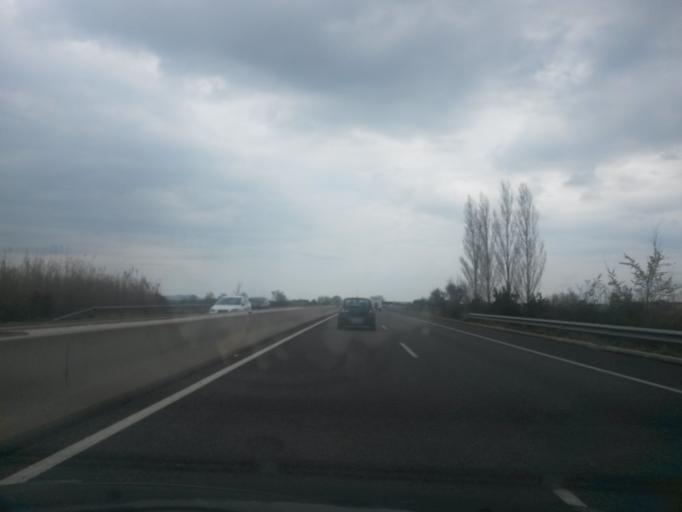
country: ES
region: Catalonia
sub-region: Provincia de Girona
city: Vila-sacra
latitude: 42.2663
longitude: 3.0300
